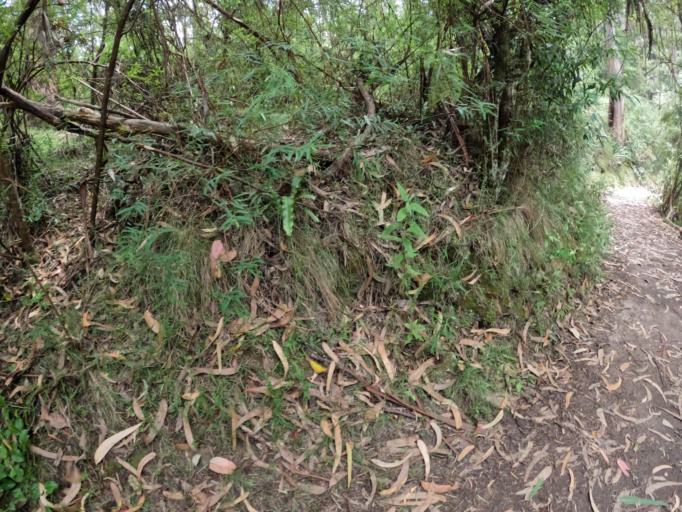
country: AU
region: Victoria
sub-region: Colac-Otway
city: Apollo Bay
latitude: -38.7898
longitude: 143.6202
